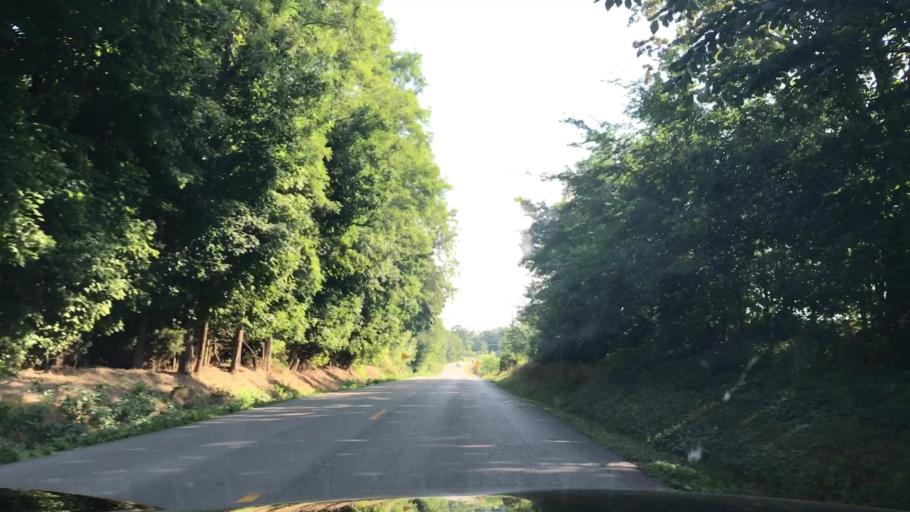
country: US
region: Kentucky
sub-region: Hart County
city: Horse Cave
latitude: 37.1721
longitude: -85.7933
